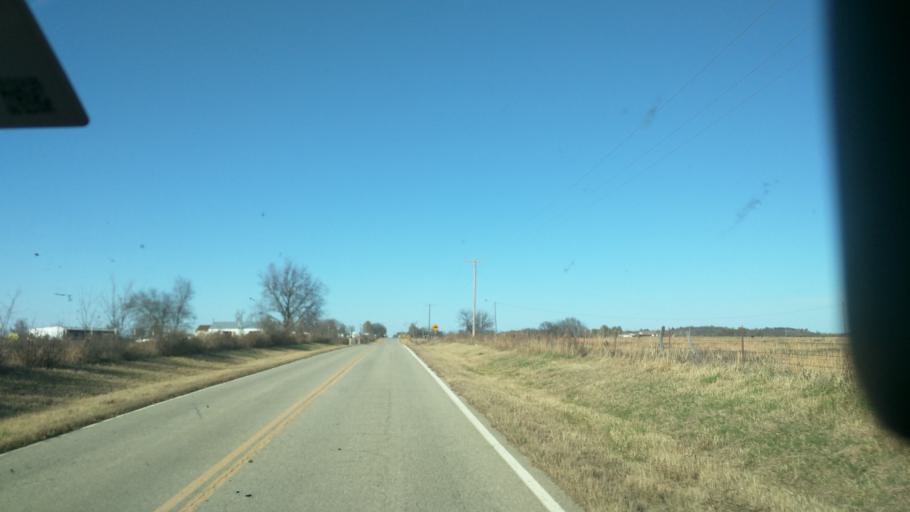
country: US
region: Oklahoma
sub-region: Nowata County
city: Nowata
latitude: 36.7662
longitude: -95.5396
